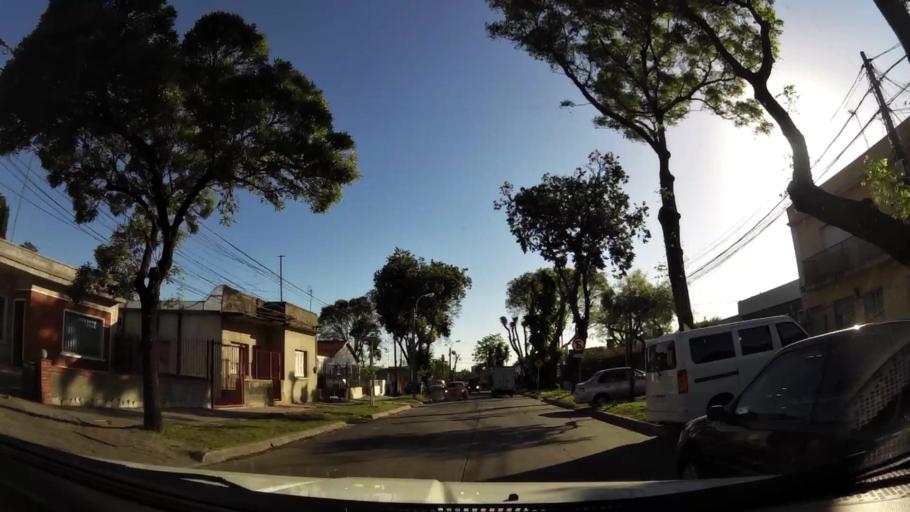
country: UY
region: Montevideo
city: Montevideo
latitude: -34.8353
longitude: -56.2124
